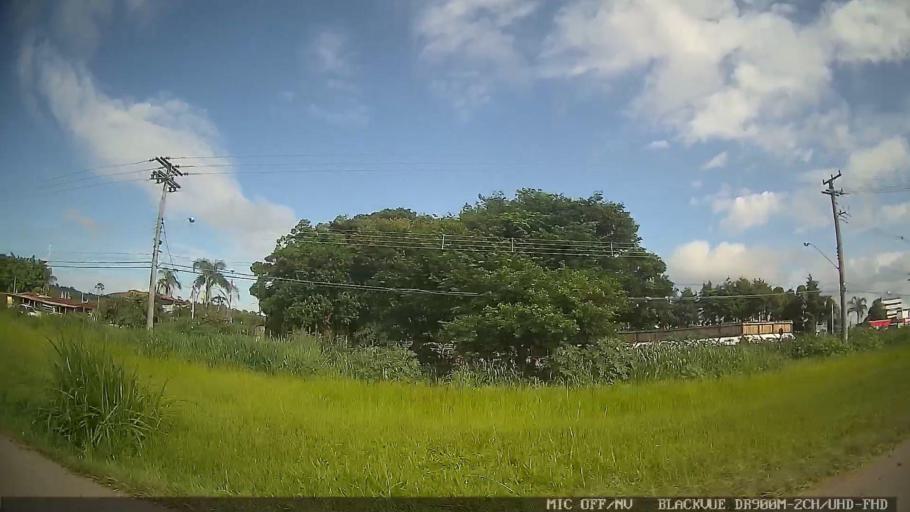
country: BR
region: Sao Paulo
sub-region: Jarinu
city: Jarinu
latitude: -23.0489
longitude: -46.6753
